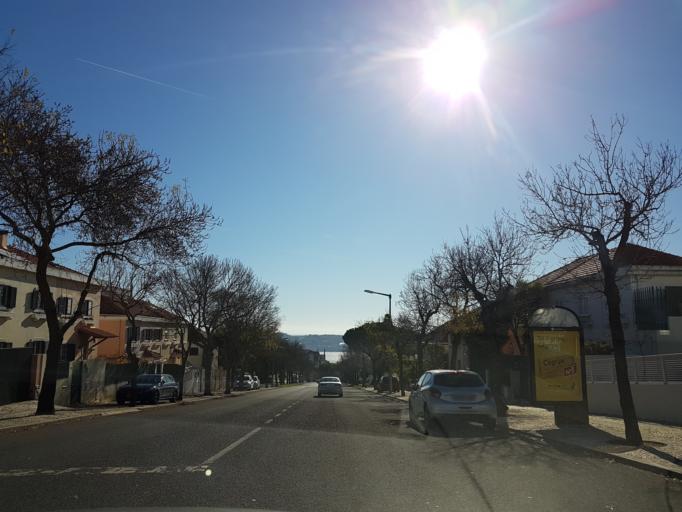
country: PT
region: Lisbon
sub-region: Oeiras
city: Alges
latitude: 38.7110
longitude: -9.2008
